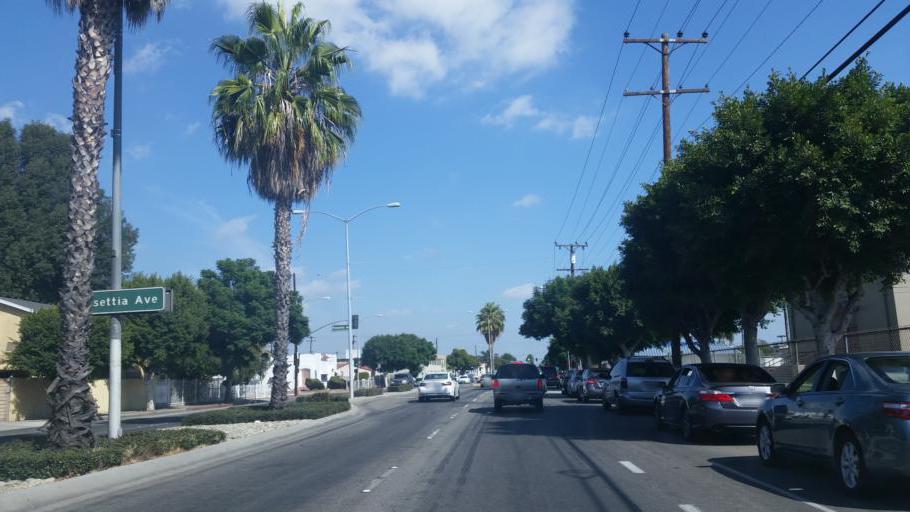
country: US
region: California
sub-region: Los Angeles County
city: Compton
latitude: 33.8886
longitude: -118.2099
